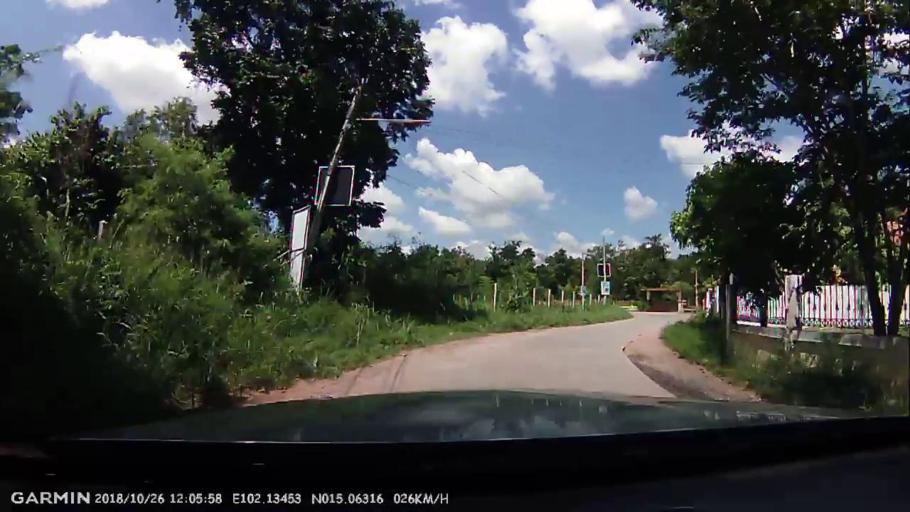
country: TH
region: Nakhon Ratchasima
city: Nakhon Ratchasima
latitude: 15.0632
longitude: 102.1346
